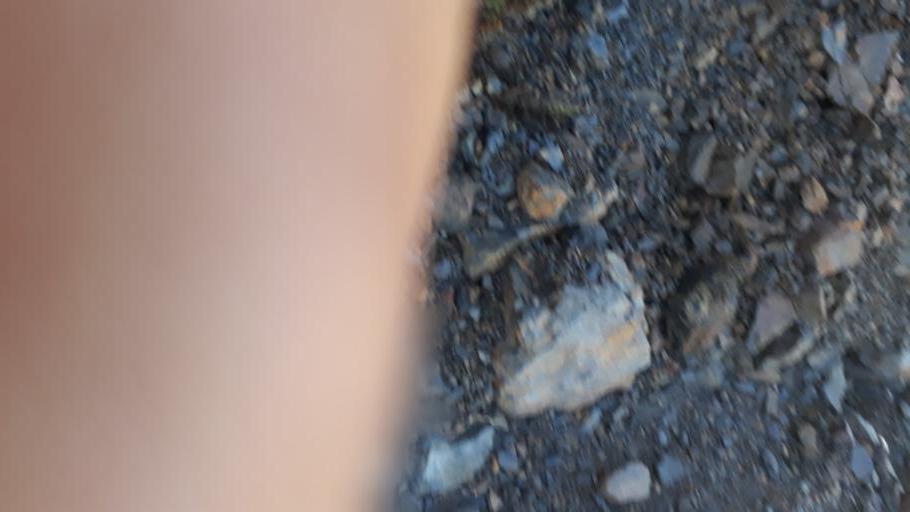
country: CO
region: Casanare
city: Nunchia
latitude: 5.6679
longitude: -72.4287
